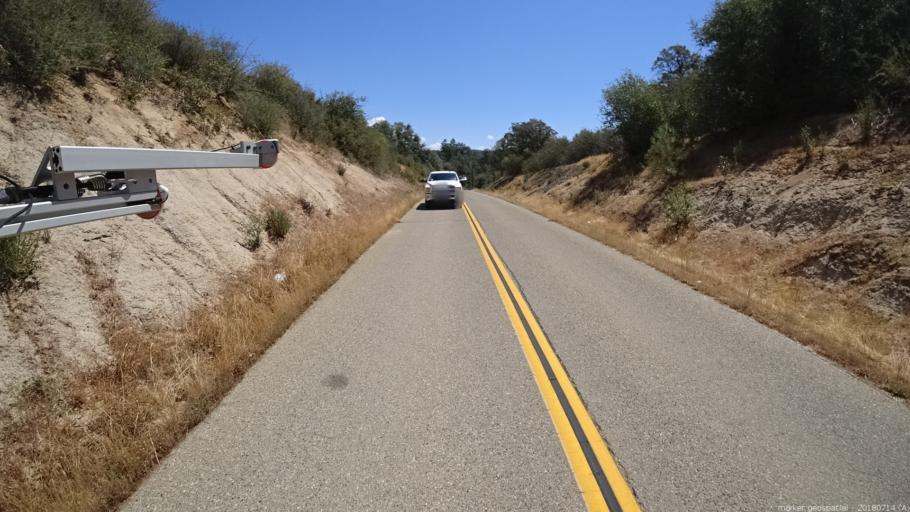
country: US
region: California
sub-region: Madera County
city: Ahwahnee
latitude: 37.3852
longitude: -119.6808
